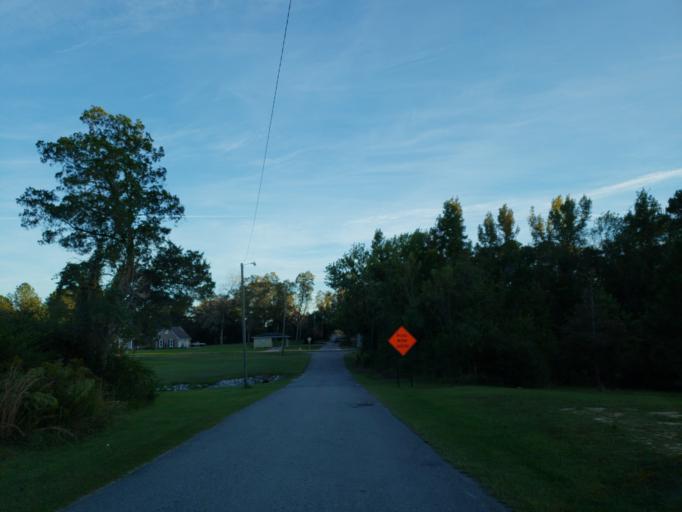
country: US
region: Mississippi
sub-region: Wayne County
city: Belmont
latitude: 31.4353
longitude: -88.4760
